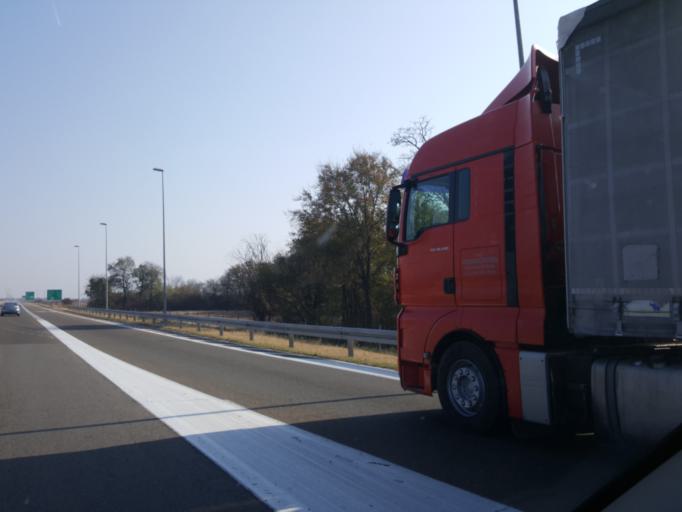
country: RS
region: Central Serbia
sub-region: Nisavski Okrug
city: Nis
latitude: 43.3557
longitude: 21.8292
